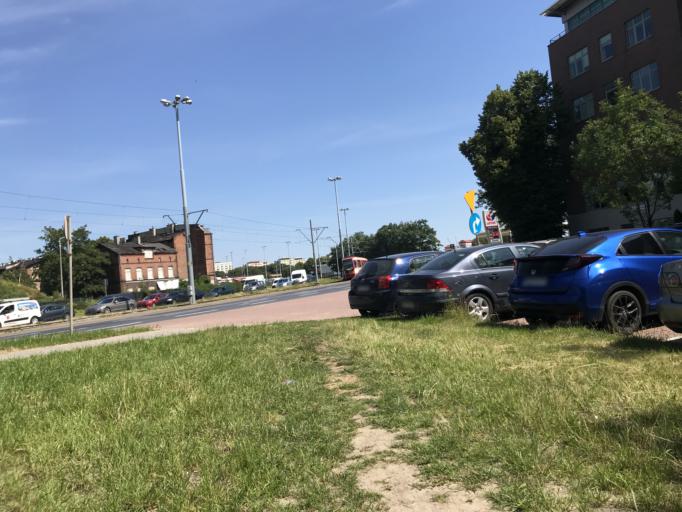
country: PL
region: Pomeranian Voivodeship
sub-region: Gdansk
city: Gdansk
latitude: 54.3449
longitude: 18.6673
